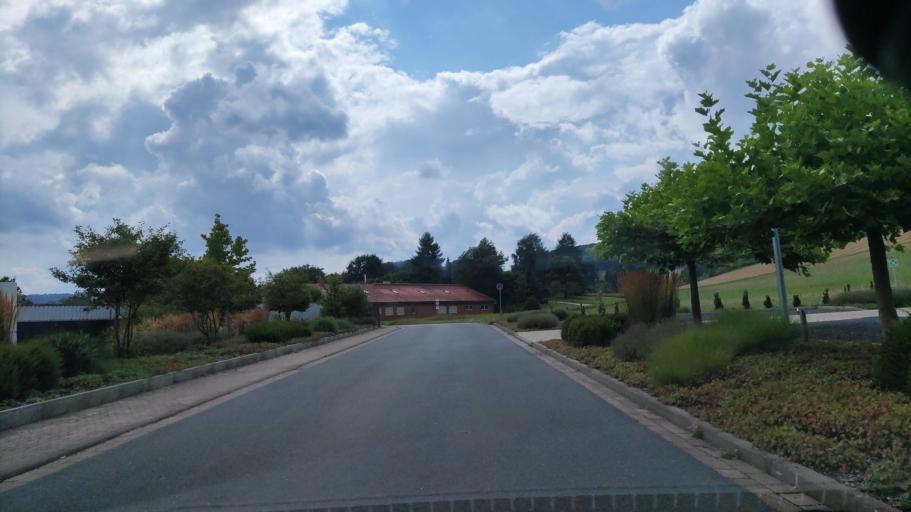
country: DE
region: Lower Saxony
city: Delligsen
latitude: 51.9380
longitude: 9.7839
